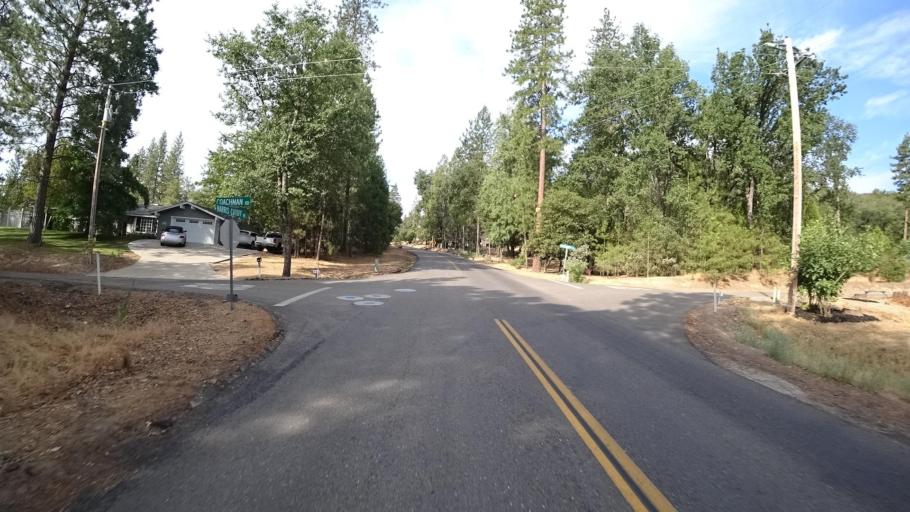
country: US
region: California
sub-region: Madera County
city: Ahwahnee
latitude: 37.4641
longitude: -119.7408
